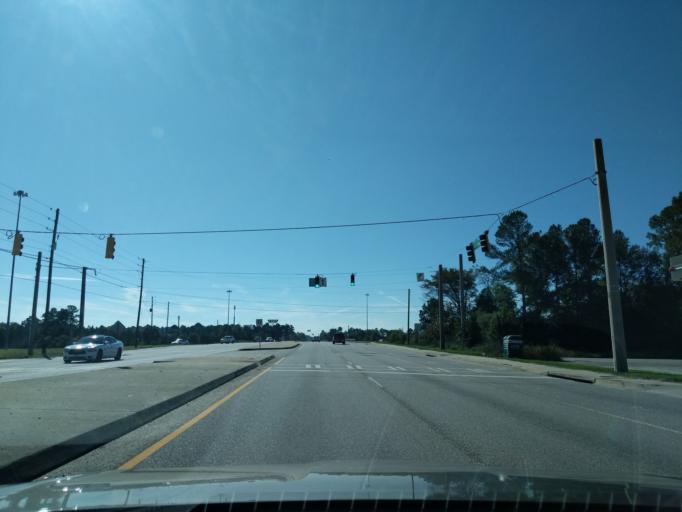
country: US
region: Georgia
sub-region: Richmond County
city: Augusta
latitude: 33.4034
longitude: -82.0060
